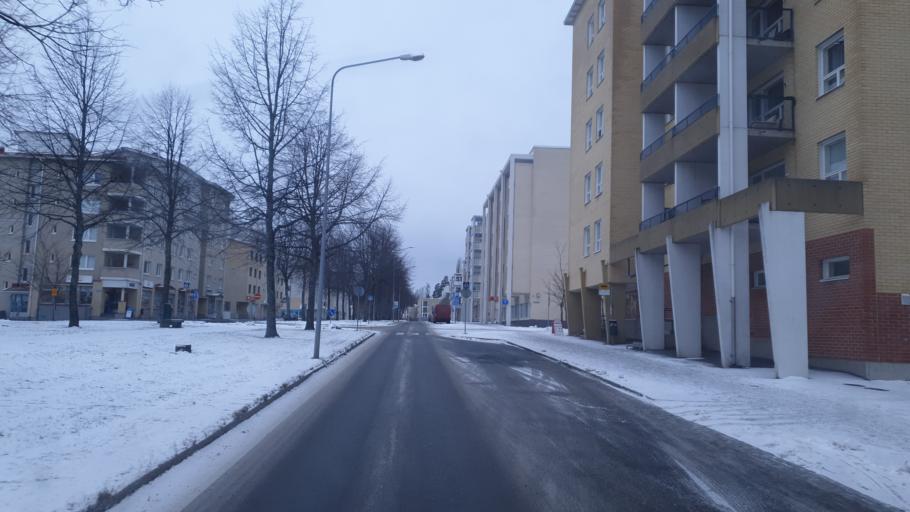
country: FI
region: Northern Savo
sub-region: Kuopio
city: Kuopio
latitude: 62.8390
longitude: 27.6410
